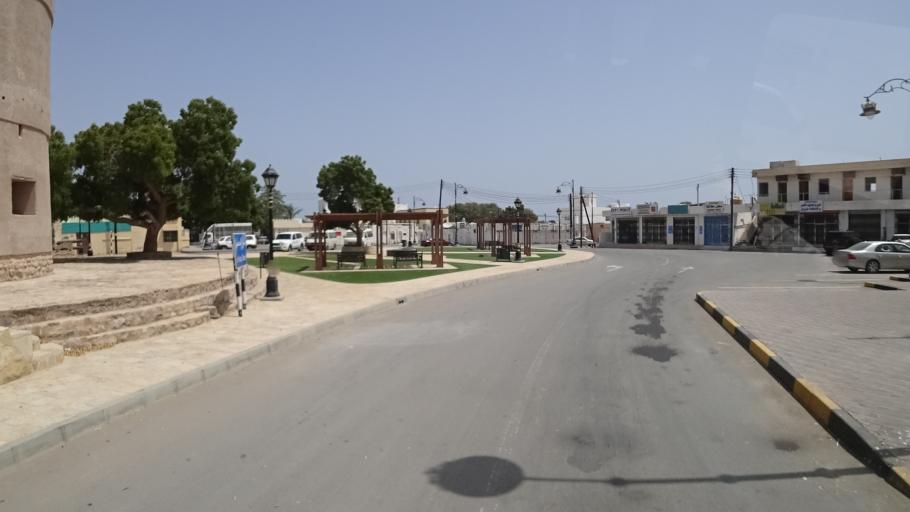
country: OM
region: Muhafazat Masqat
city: Muscat
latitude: 23.2651
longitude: 58.9158
